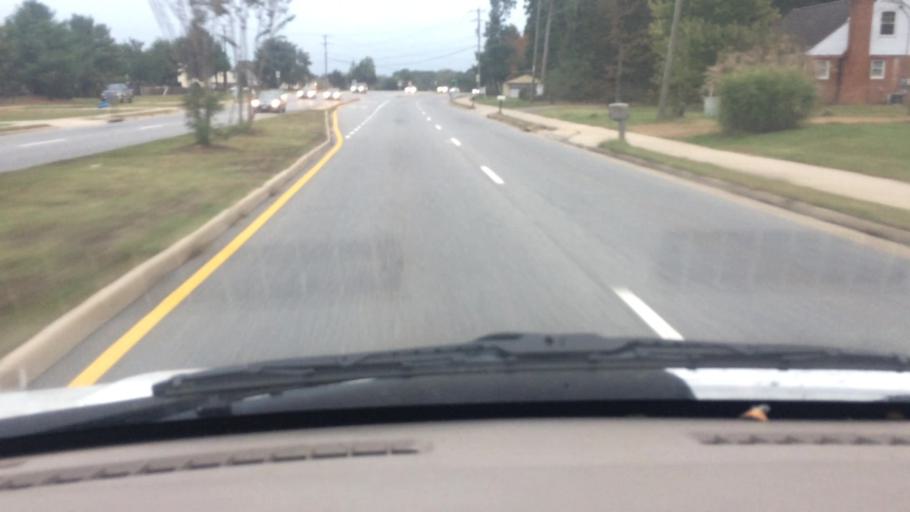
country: US
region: Virginia
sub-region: Spotsylvania County
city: Spotsylvania
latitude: 38.2497
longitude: -77.5294
